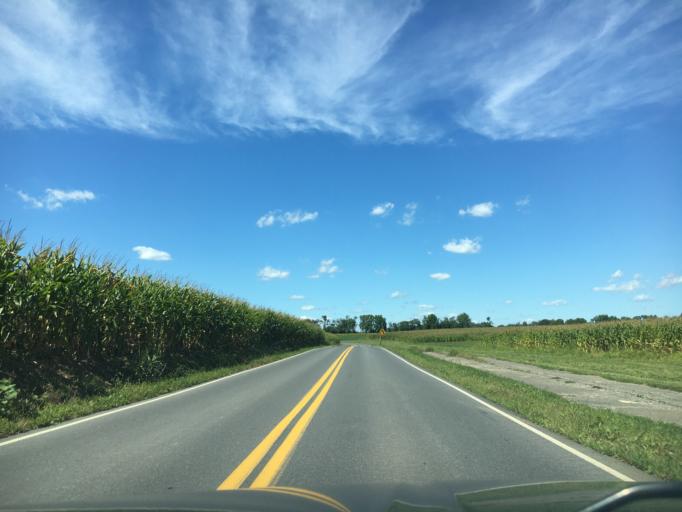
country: US
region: Pennsylvania
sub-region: Berks County
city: Topton
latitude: 40.5100
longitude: -75.6843
